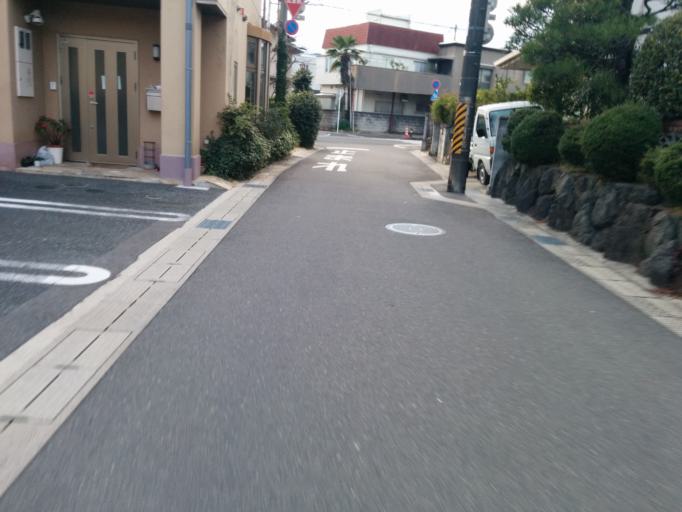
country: JP
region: Kyoto
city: Muko
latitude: 34.9360
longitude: 135.7014
